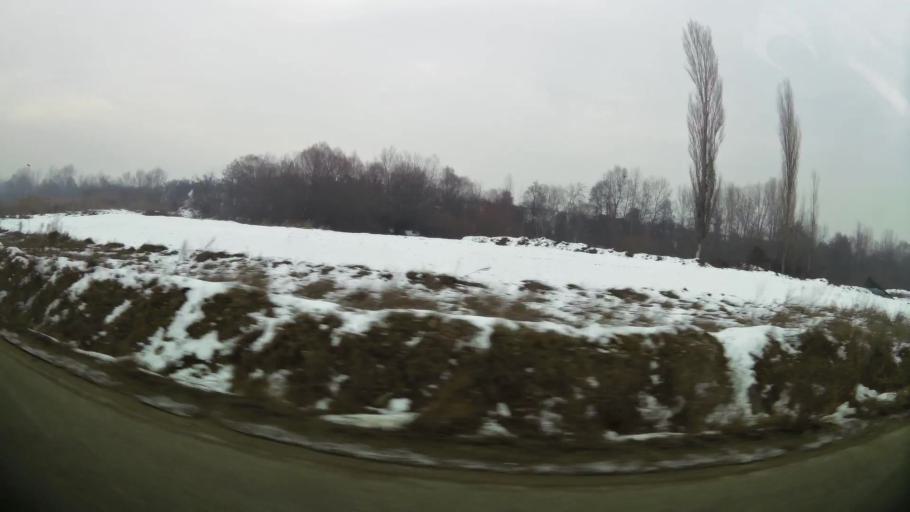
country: MK
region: Cucer-Sandevo
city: Chucher - Sandevo
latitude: 42.0484
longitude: 21.3659
